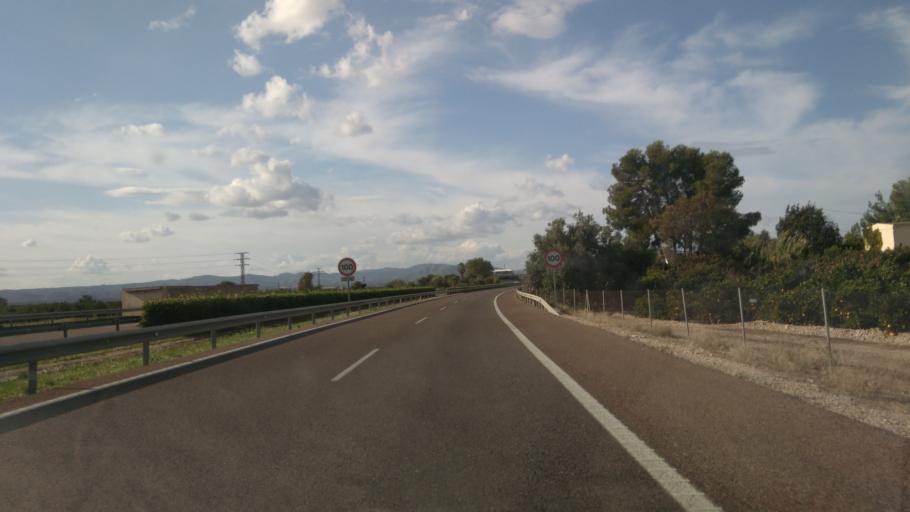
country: ES
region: Valencia
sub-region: Provincia de Valencia
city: Guadassuar
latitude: 39.1792
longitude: -0.4830
